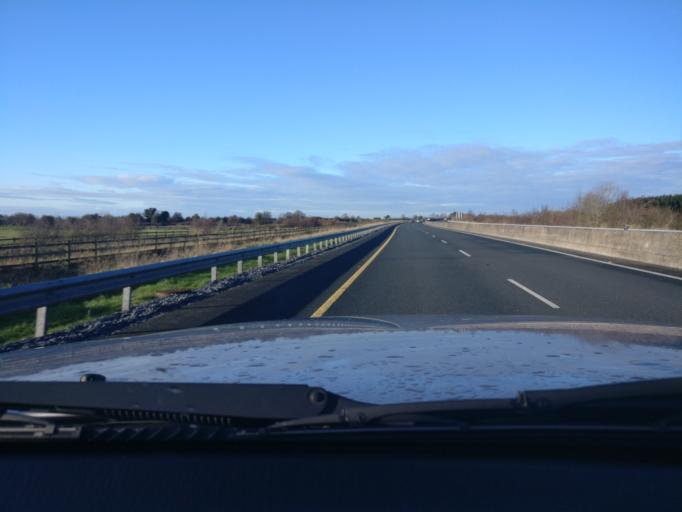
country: IE
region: Connaught
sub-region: County Galway
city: Athenry
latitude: 53.2705
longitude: -8.6576
